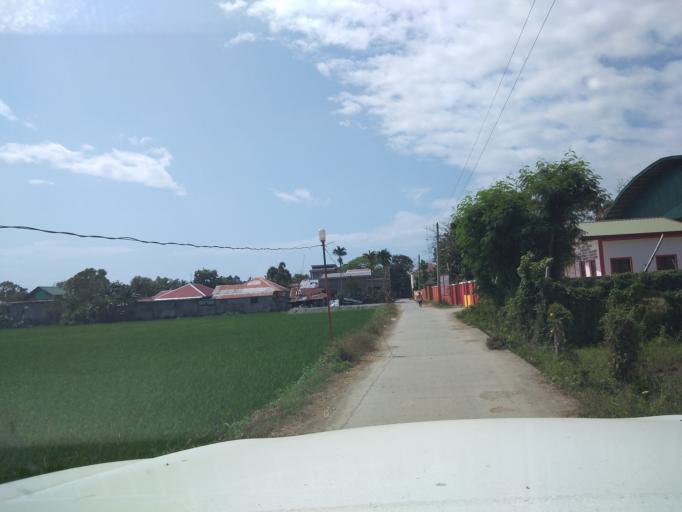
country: PH
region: Central Luzon
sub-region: Province of Pampanga
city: Talang
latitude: 15.0283
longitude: 120.8344
